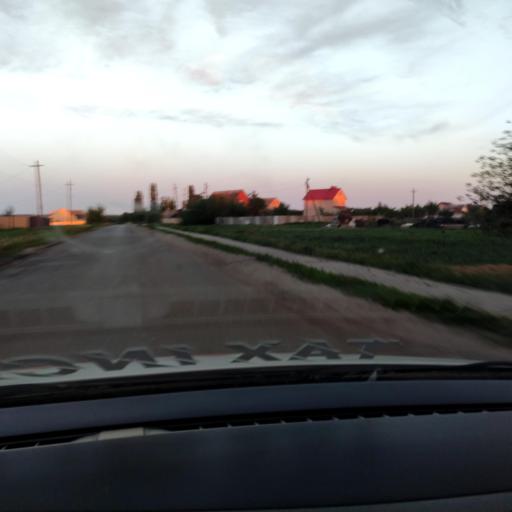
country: RU
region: Voronezj
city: Maslovka
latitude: 51.4560
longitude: 39.2389
